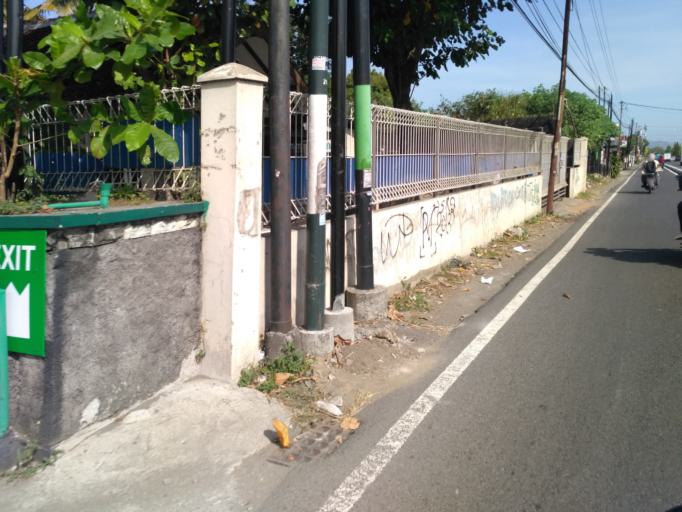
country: ID
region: Daerah Istimewa Yogyakarta
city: Depok
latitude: -7.7755
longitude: 110.4306
